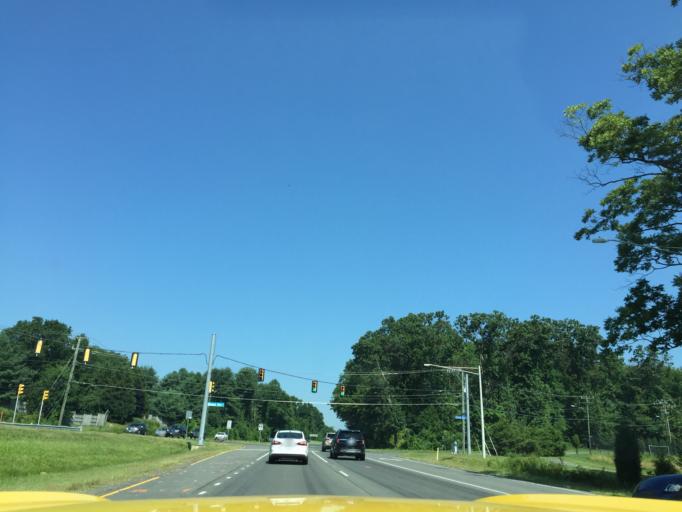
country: US
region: Virginia
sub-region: Fairfax County
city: Dranesville
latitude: 38.9891
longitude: -77.3286
